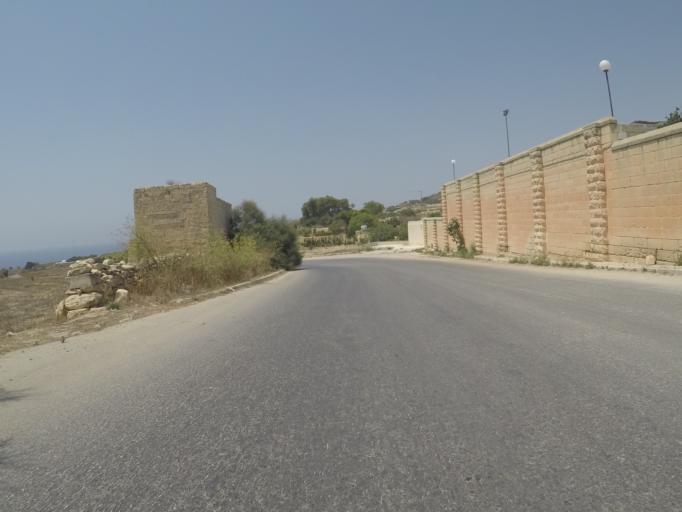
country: MT
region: Is-Siggiewi
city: Siggiewi
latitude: 35.8362
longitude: 14.4258
